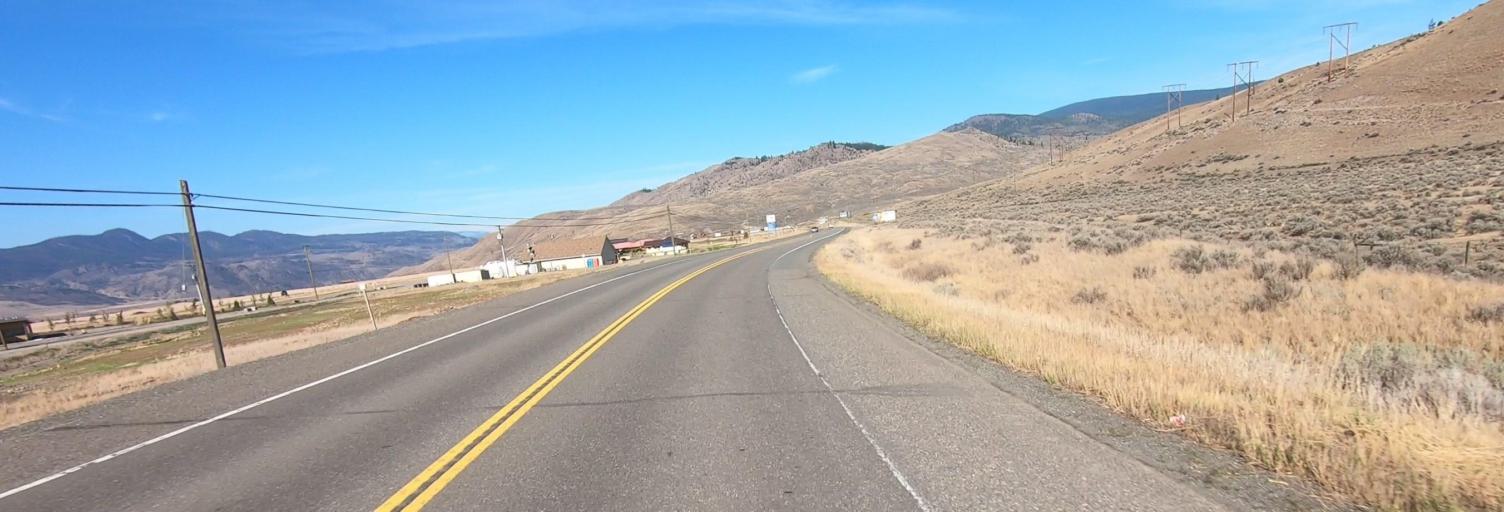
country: CA
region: British Columbia
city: Logan Lake
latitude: 50.7703
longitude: -120.9361
